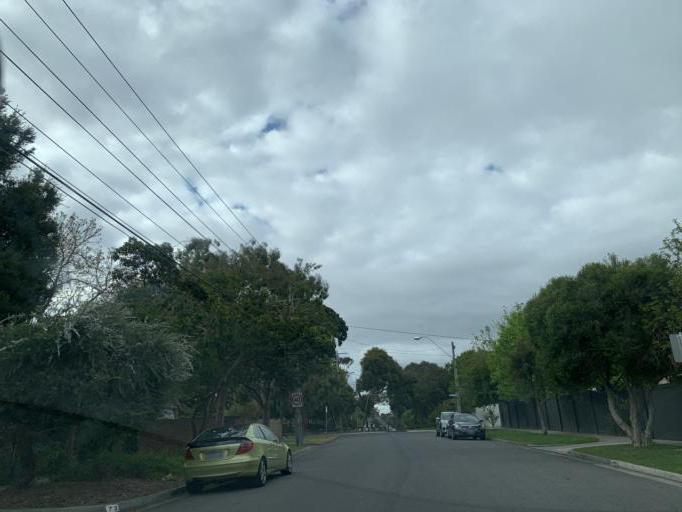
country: AU
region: Victoria
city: Beaumaris
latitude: -37.9865
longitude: 145.0377
